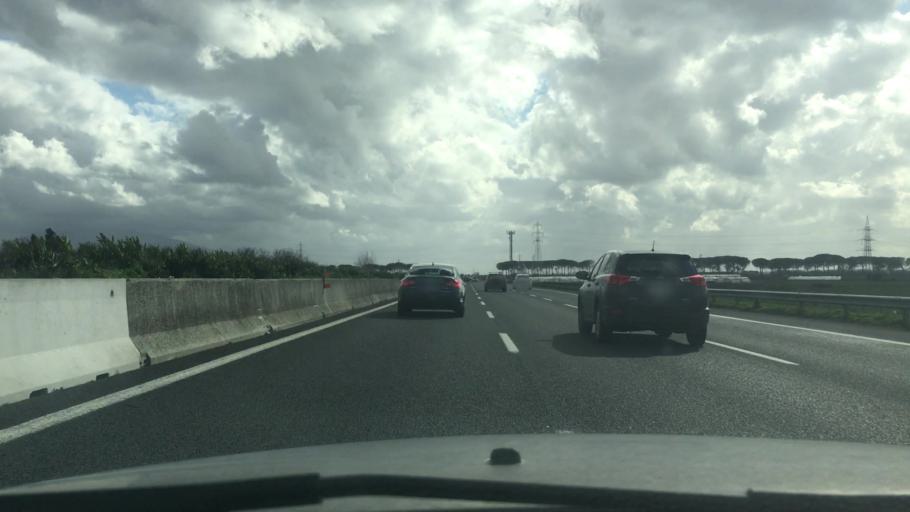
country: IT
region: Campania
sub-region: Provincia di Napoli
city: Pascarola
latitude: 40.9953
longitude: 14.3244
